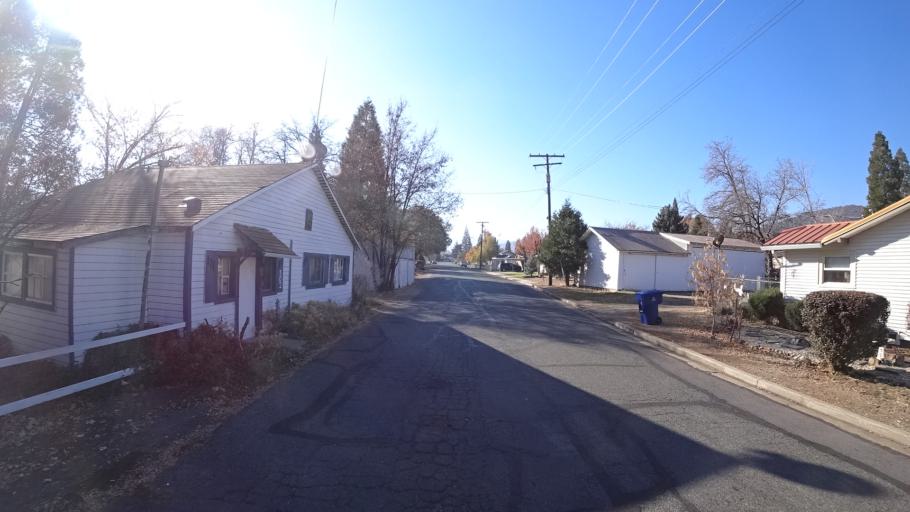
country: US
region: California
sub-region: Siskiyou County
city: Yreka
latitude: 41.7316
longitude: -122.6441
